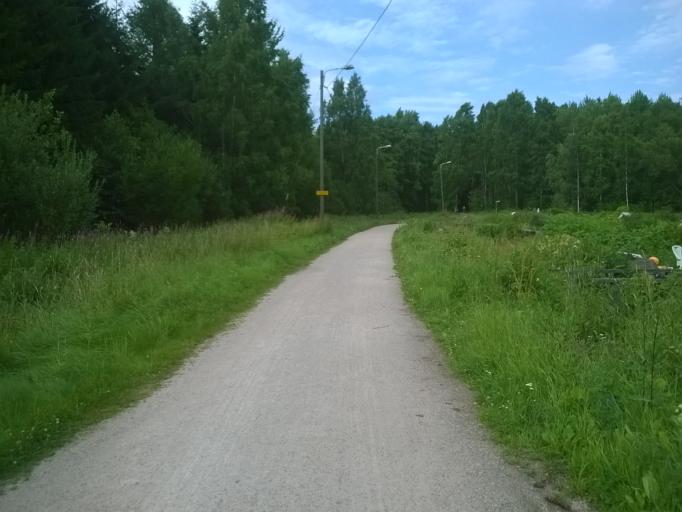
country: FI
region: Uusimaa
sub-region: Helsinki
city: Helsinki
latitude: 60.2263
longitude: 24.9116
